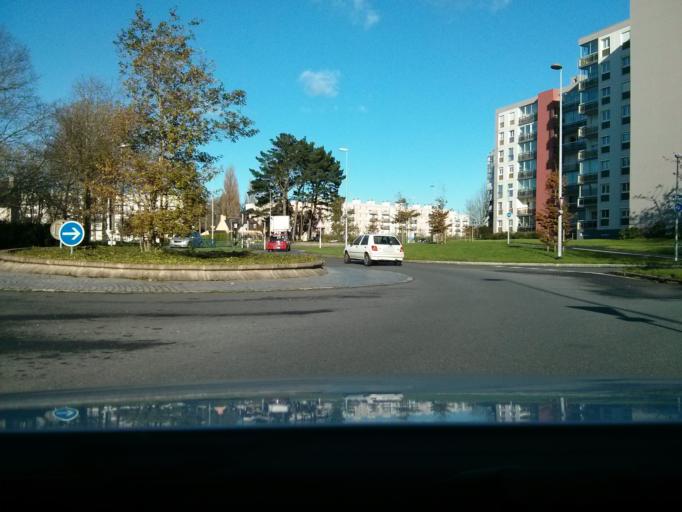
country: FR
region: Brittany
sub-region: Departement du Finistere
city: Bohars
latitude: 48.4068
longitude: -4.5224
